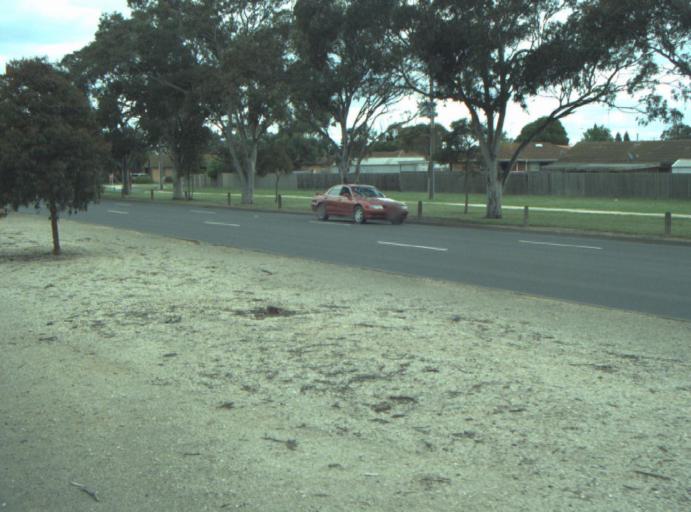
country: AU
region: Victoria
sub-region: Greater Geelong
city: Lara
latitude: -38.0664
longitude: 144.3799
